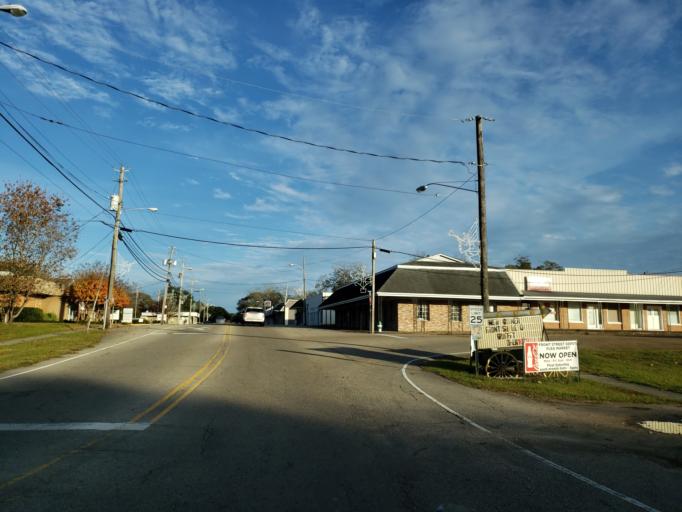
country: US
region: Mississippi
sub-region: Lamar County
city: Purvis
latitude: 31.1432
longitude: -89.4118
